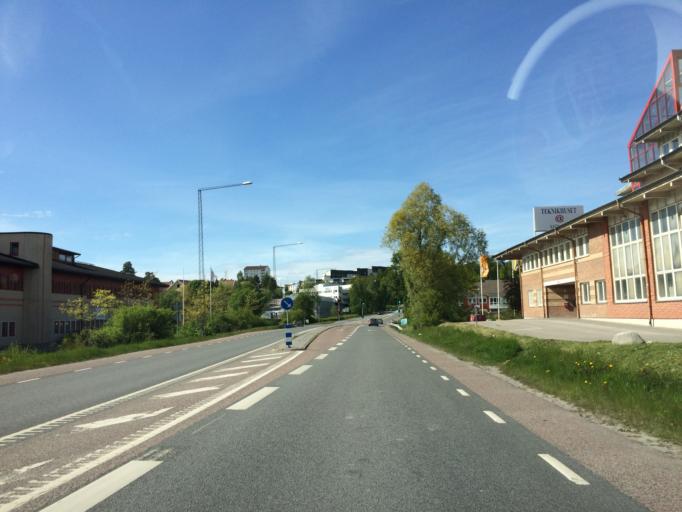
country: SE
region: Stockholm
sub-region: Sollentuna Kommun
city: Sollentuna
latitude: 59.4256
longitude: 17.9993
